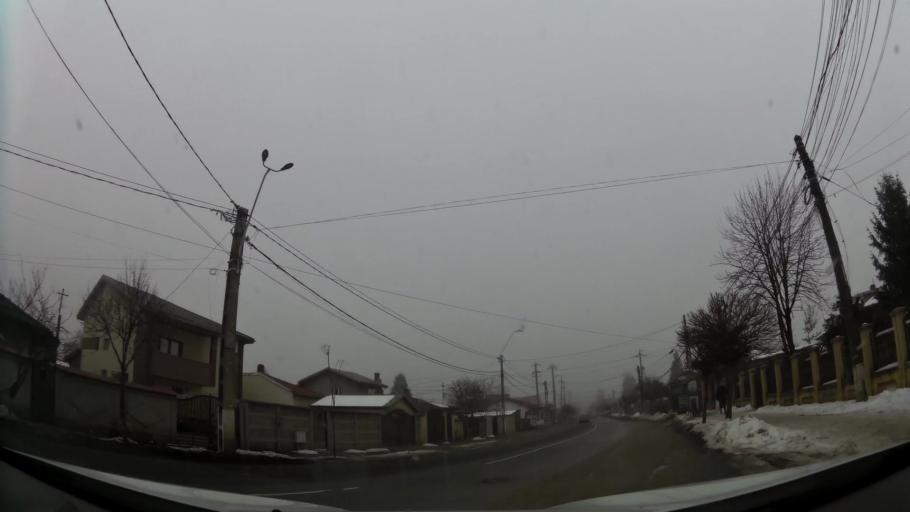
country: RO
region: Ilfov
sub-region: Comuna Chiajna
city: Chiajna
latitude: 44.4545
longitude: 25.9882
